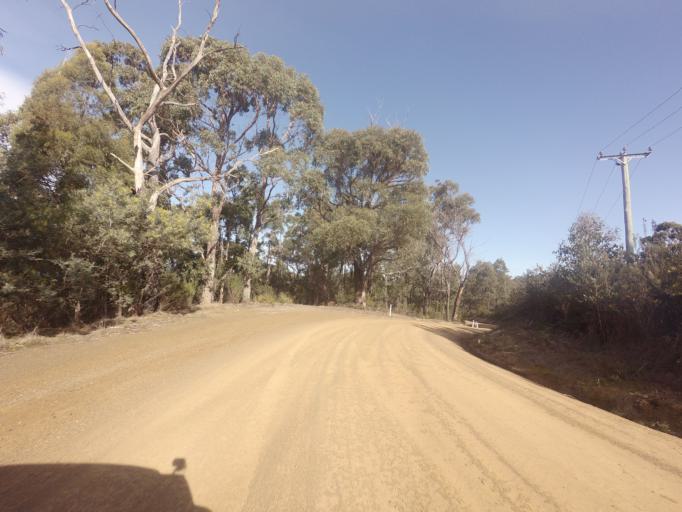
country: AU
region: Tasmania
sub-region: Kingborough
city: Kettering
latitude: -43.0941
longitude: 147.2638
